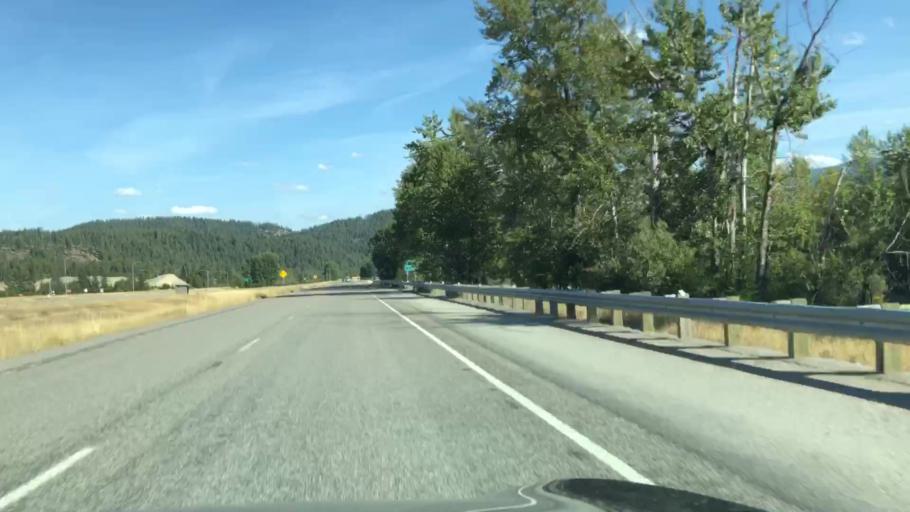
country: US
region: Montana
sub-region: Sanders County
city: Thompson Falls
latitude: 47.3932
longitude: -115.4248
